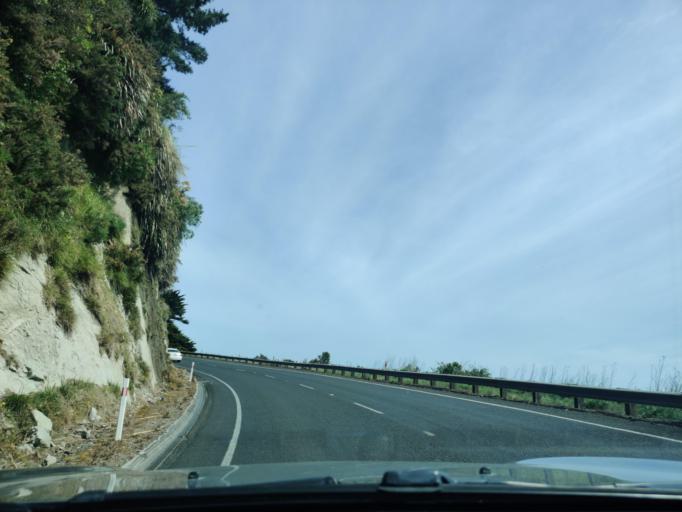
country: NZ
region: Taranaki
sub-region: South Taranaki District
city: Hawera
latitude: -39.6444
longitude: 174.3761
